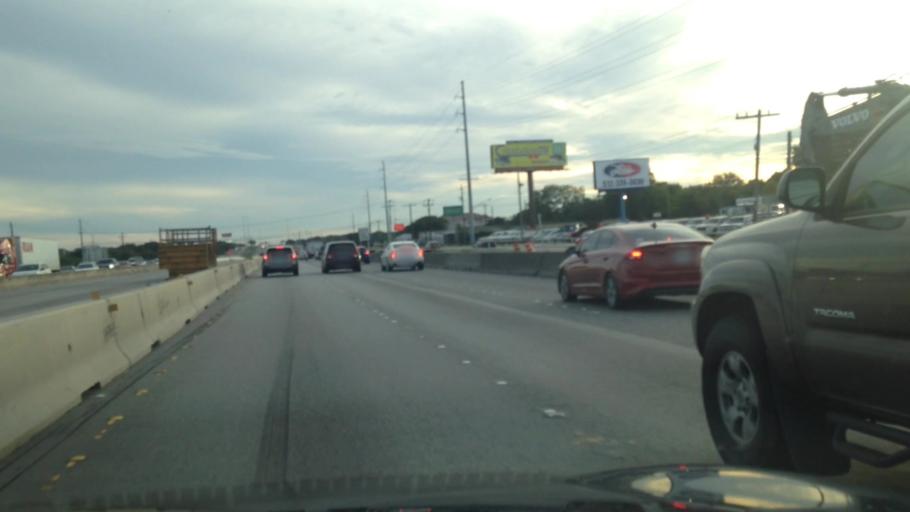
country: US
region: Texas
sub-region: Travis County
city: Onion Creek
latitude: 30.1868
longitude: -97.7732
